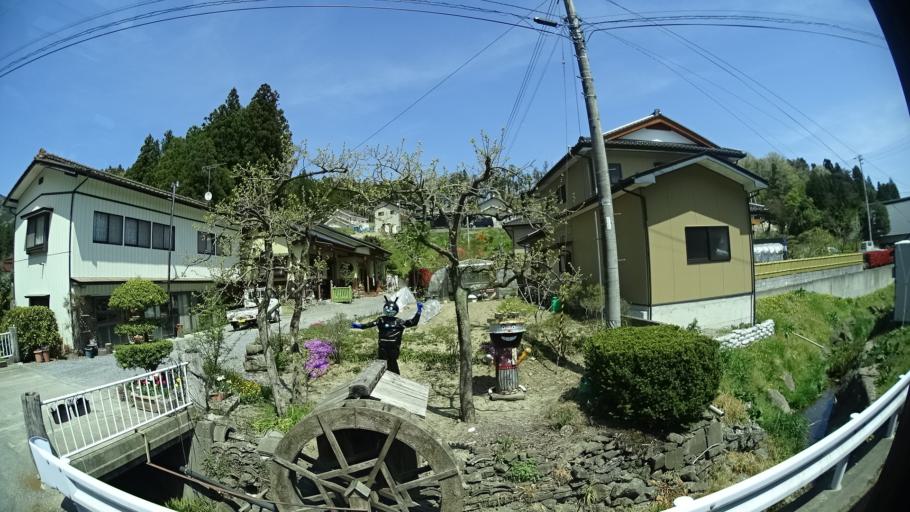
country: JP
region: Iwate
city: Ofunato
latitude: 39.0195
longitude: 141.6623
